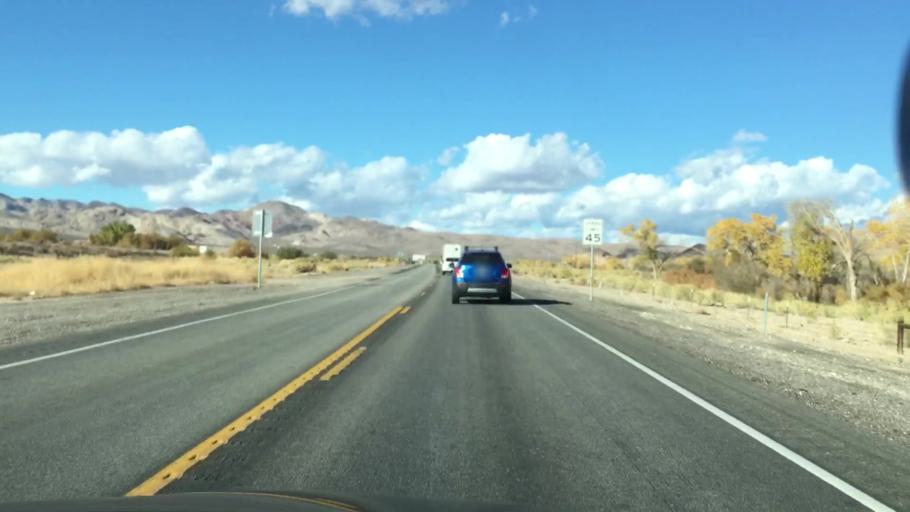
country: US
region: Nevada
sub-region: Nye County
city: Beatty
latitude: 36.8952
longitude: -116.7520
